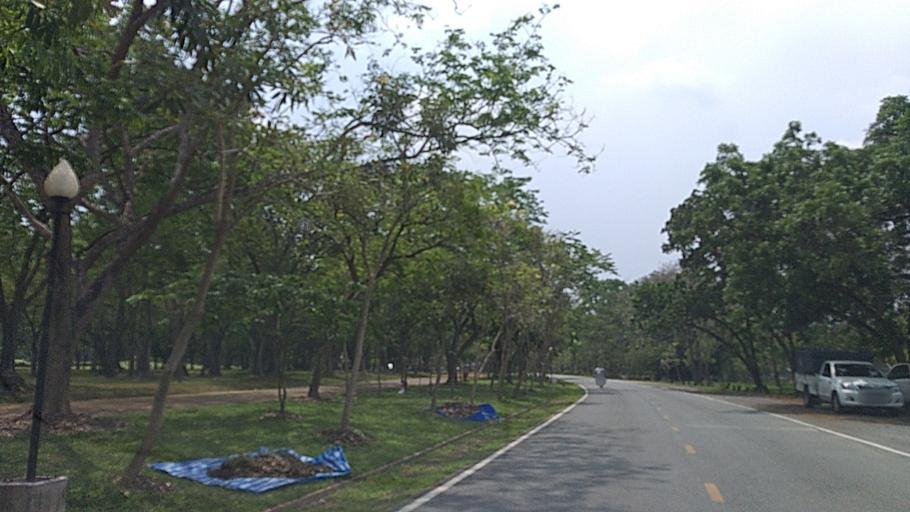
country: TH
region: Bangkok
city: Thawi Watthana
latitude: 13.7766
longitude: 100.3171
